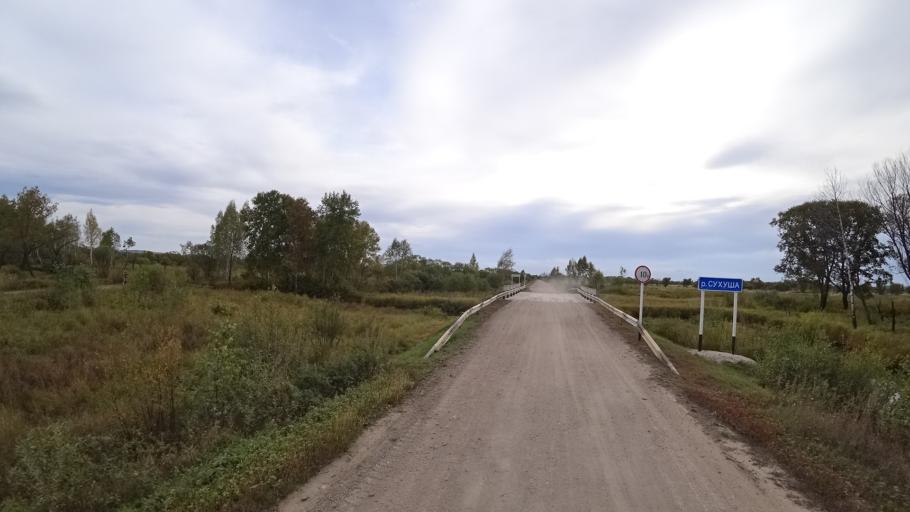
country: RU
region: Amur
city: Arkhara
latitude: 49.3786
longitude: 130.2130
